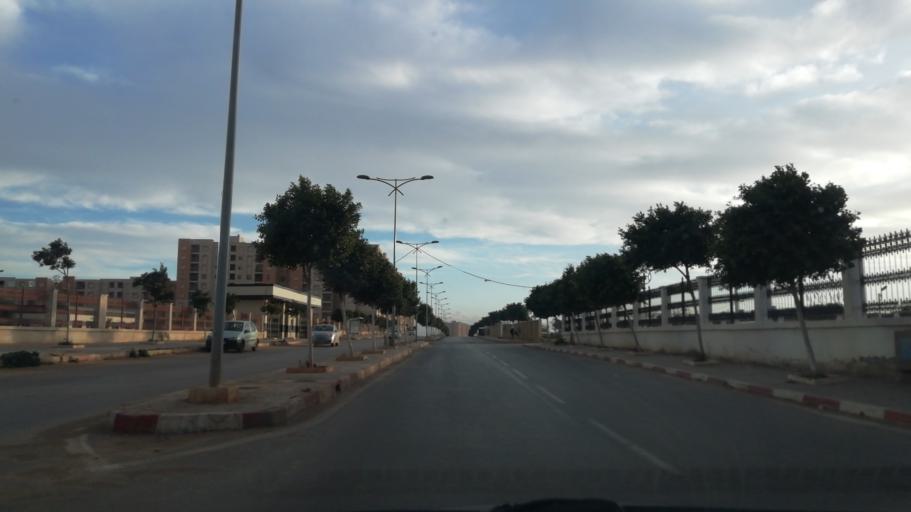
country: DZ
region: Oran
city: Bir el Djir
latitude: 35.6944
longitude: -0.5856
